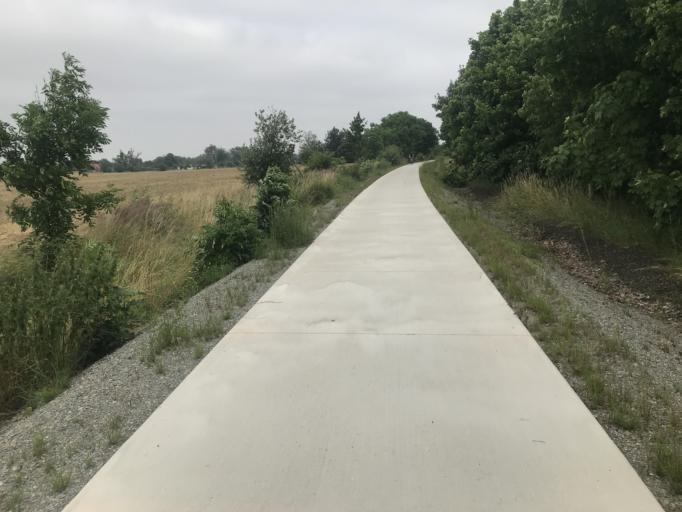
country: DE
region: Saxony-Anhalt
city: Ballenstedt
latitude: 51.7250
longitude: 11.2182
